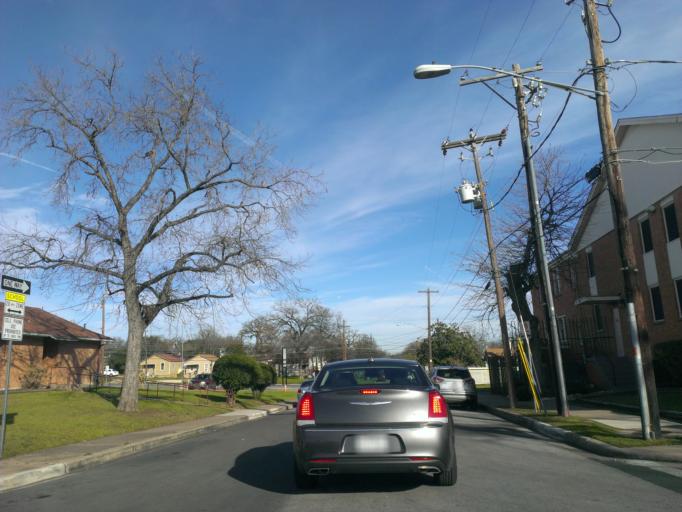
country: US
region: Texas
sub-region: Travis County
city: Austin
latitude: 30.2716
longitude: -97.7205
